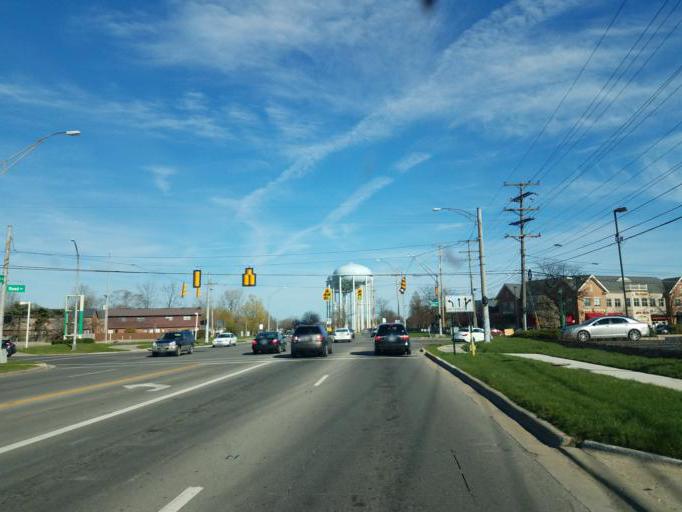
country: US
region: Ohio
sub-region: Franklin County
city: Upper Arlington
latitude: 40.0542
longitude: -83.0675
